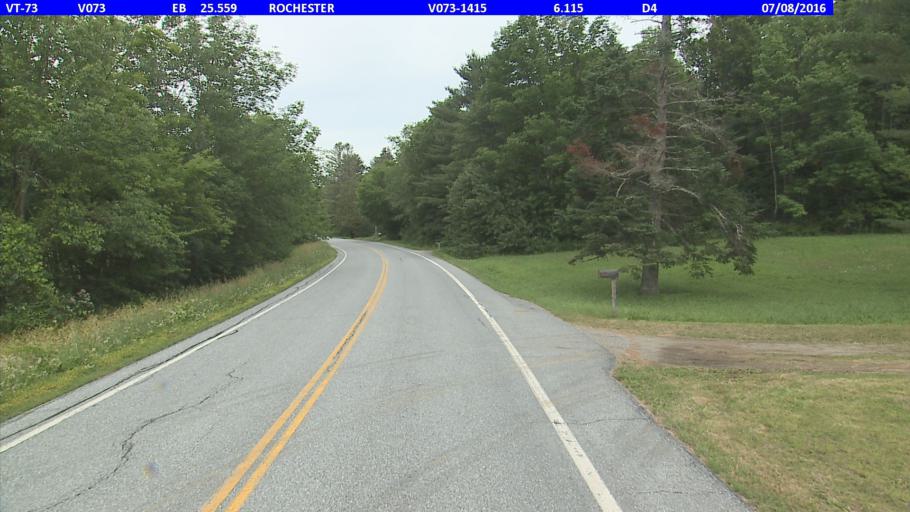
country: US
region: Vermont
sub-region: Orange County
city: Randolph
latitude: 43.8480
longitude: -72.8544
